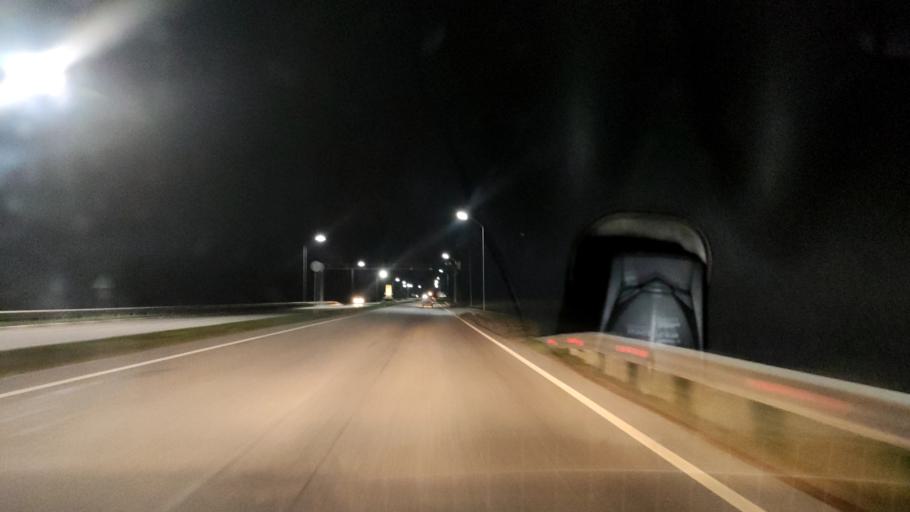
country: RU
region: Belgorod
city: Staryy Oskol
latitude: 51.4232
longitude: 37.8936
